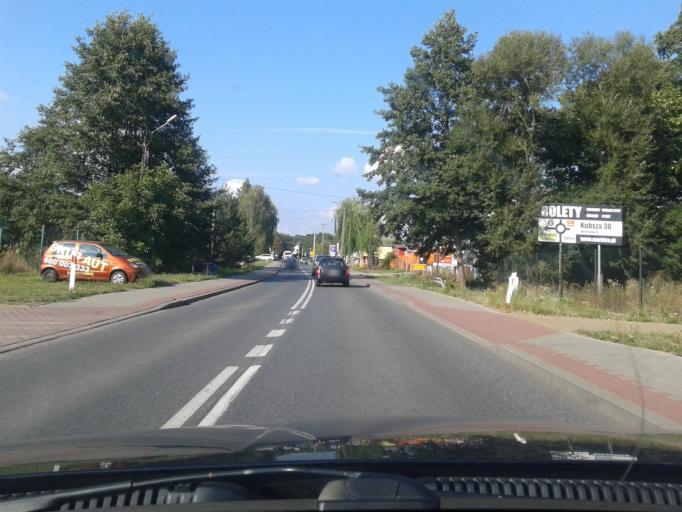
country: PL
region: Silesian Voivodeship
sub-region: Powiat wodzislawski
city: Wodzislaw Slaski
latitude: 49.9945
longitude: 18.4573
